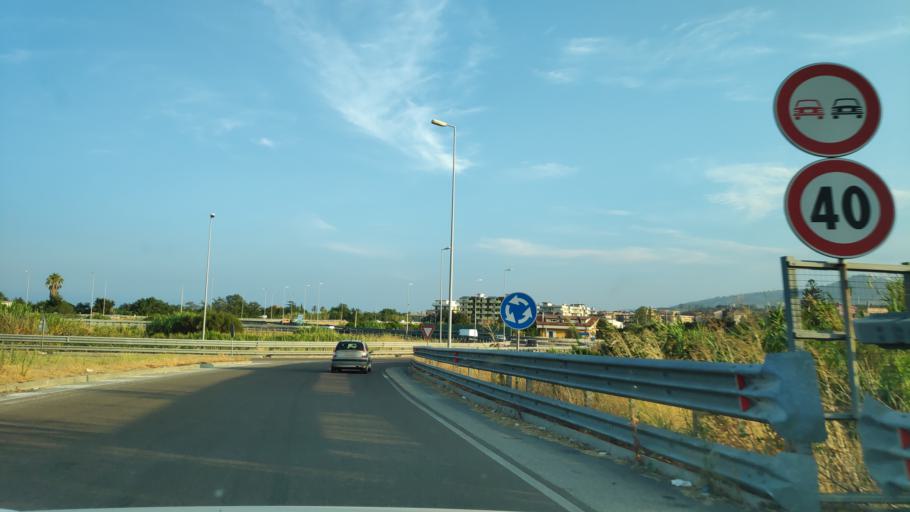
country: IT
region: Calabria
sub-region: Provincia di Catanzaro
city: Marina di Davoli
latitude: 38.6730
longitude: 16.5466
